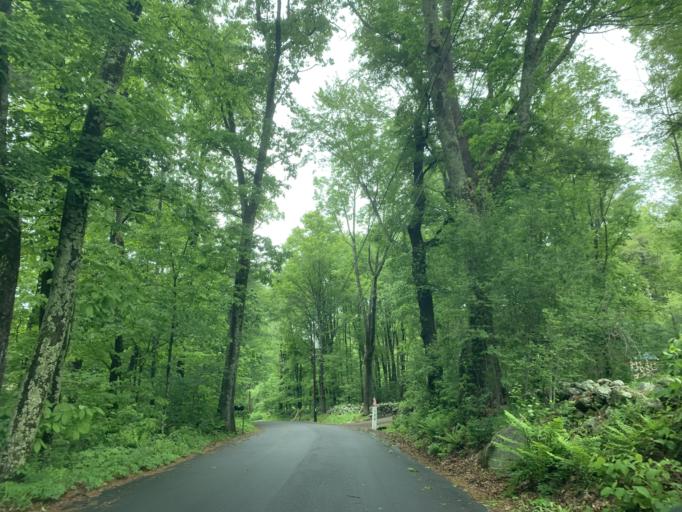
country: US
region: Massachusetts
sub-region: Worcester County
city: Upton
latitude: 42.1832
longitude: -71.6211
